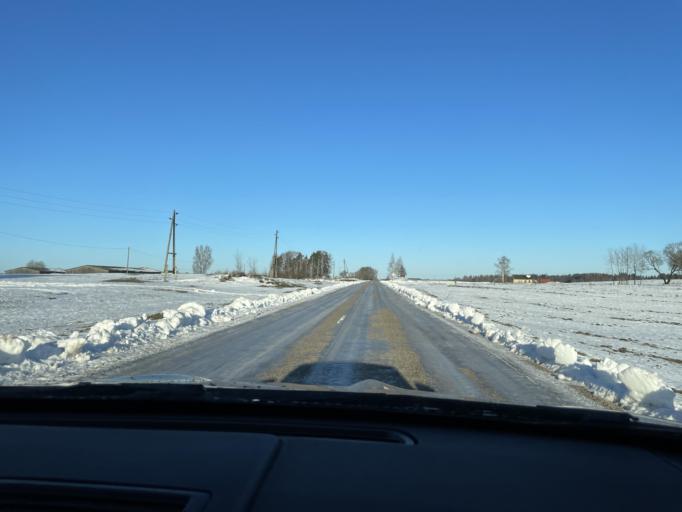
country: LV
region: Ludzas Rajons
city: Ludza
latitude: 56.4392
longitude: 27.5408
